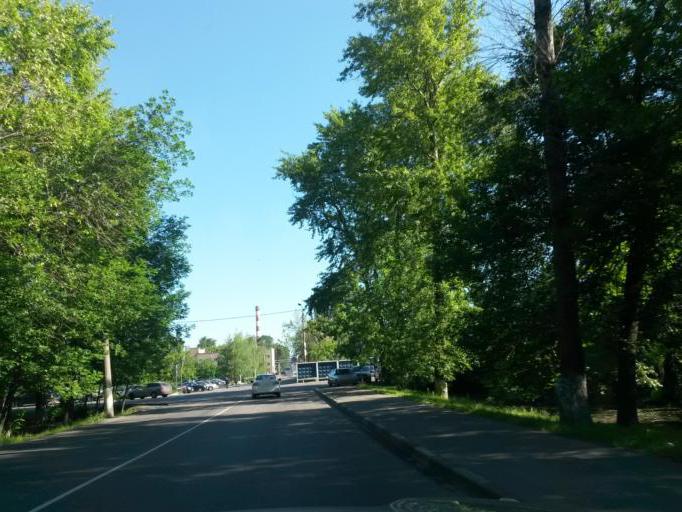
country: RU
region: Moscow
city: Kapotnya
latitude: 55.6417
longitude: 37.7992
